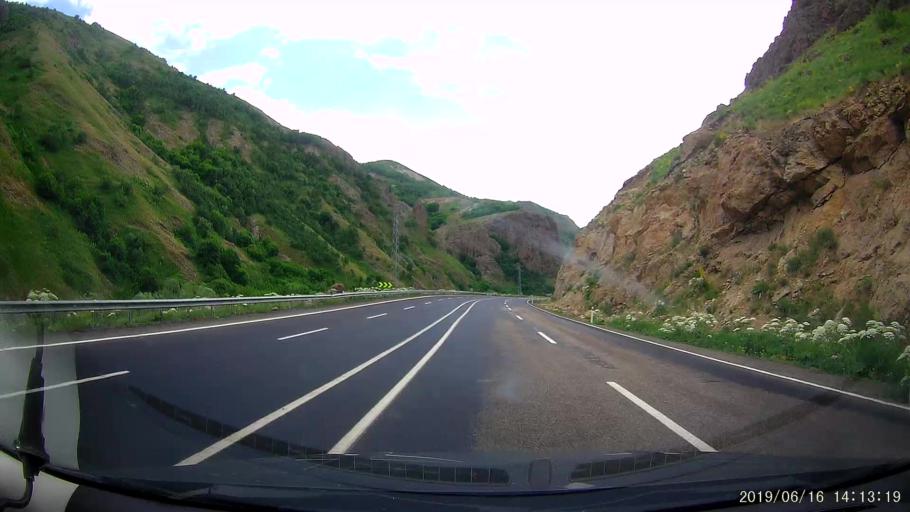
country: TR
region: Agri
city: Tahir
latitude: 39.7977
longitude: 42.5193
